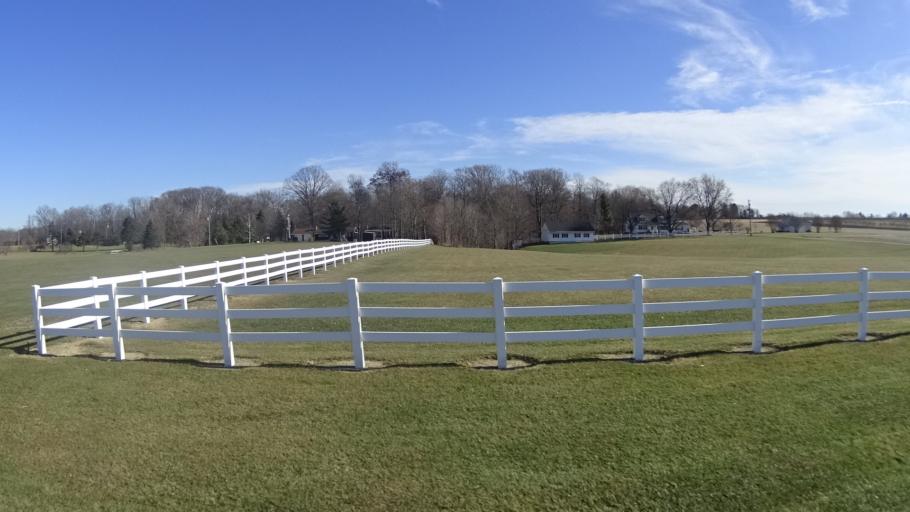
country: US
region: Ohio
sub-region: Lorain County
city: South Amherst
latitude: 41.3504
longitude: -82.2995
